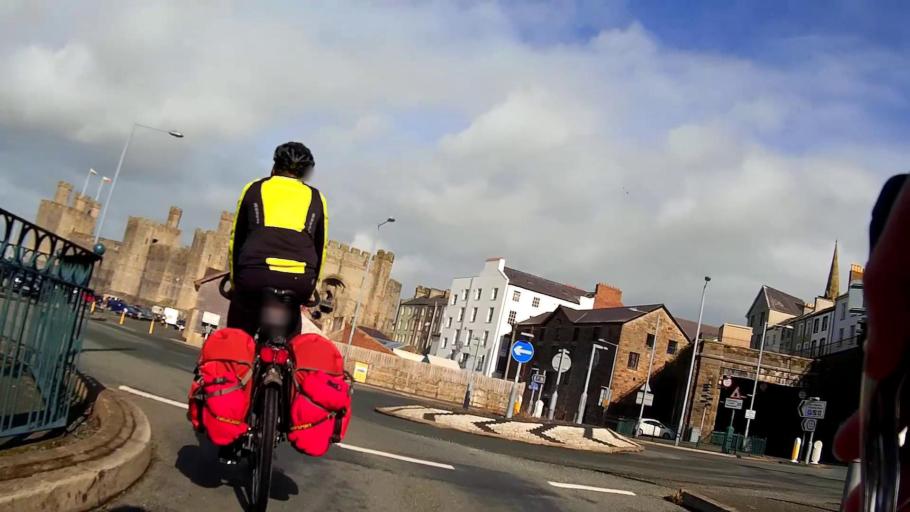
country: GB
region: Wales
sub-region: Gwynedd
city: Caernarfon
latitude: 53.1384
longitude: -4.2740
